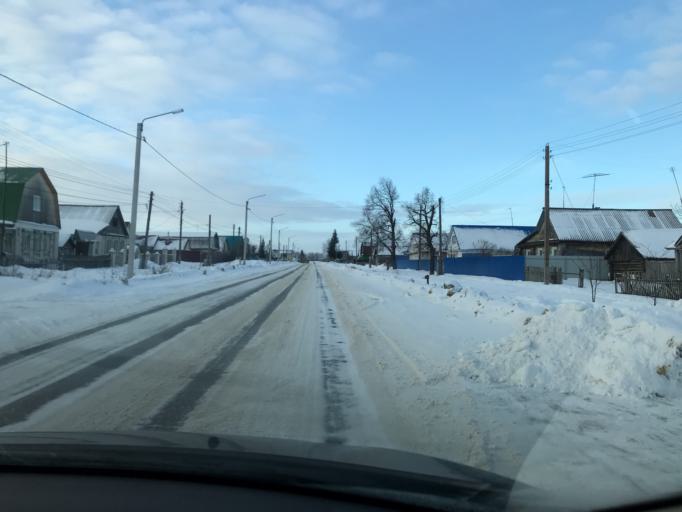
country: RU
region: Ulyanovsk
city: Undory
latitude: 54.6058
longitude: 48.4001
